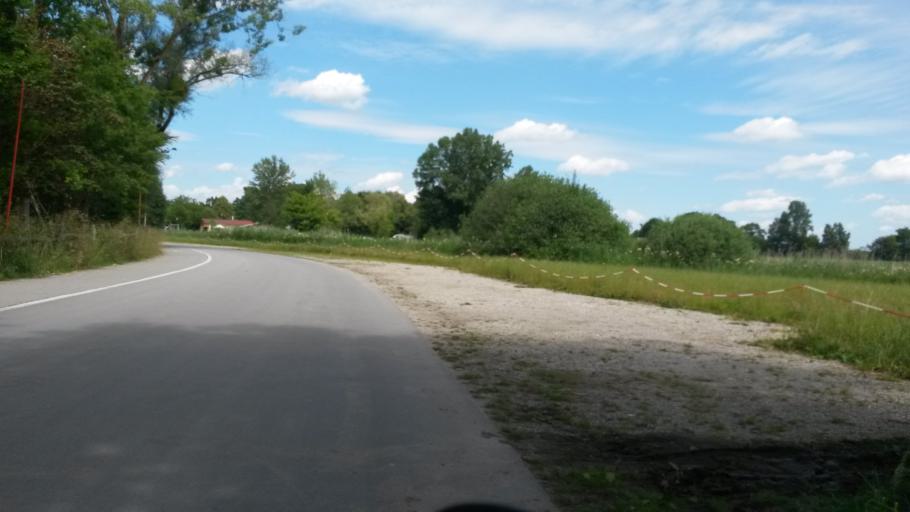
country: DE
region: Bavaria
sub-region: Upper Bavaria
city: Ubersee
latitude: 47.8470
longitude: 12.4770
